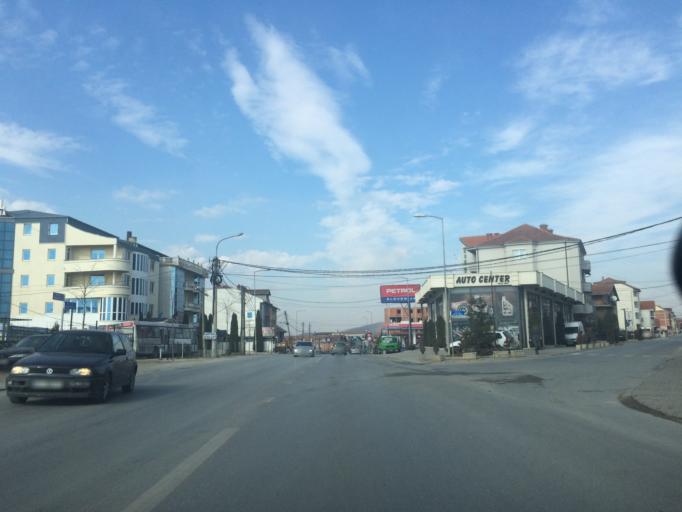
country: XK
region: Pristina
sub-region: Komuna e Prishtines
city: Pristina
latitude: 42.6870
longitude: 21.1590
